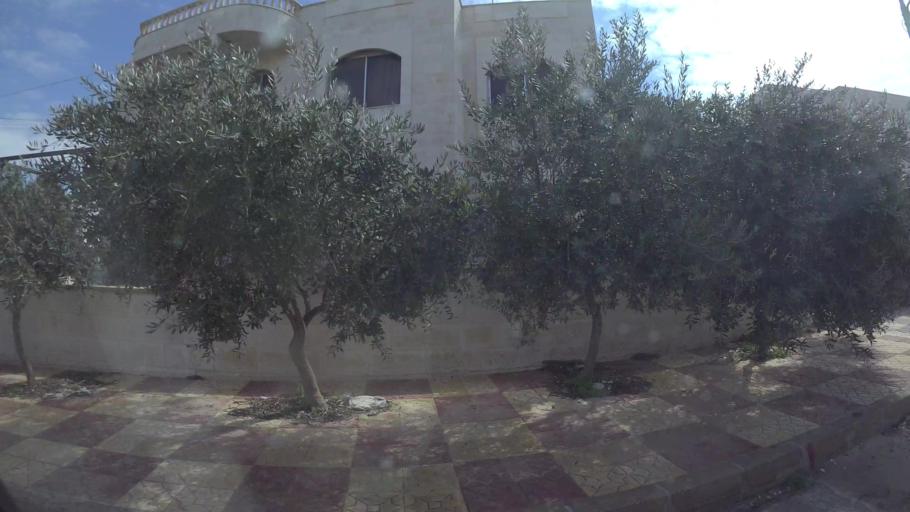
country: JO
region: Amman
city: Al Jubayhah
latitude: 32.0643
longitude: 35.8231
